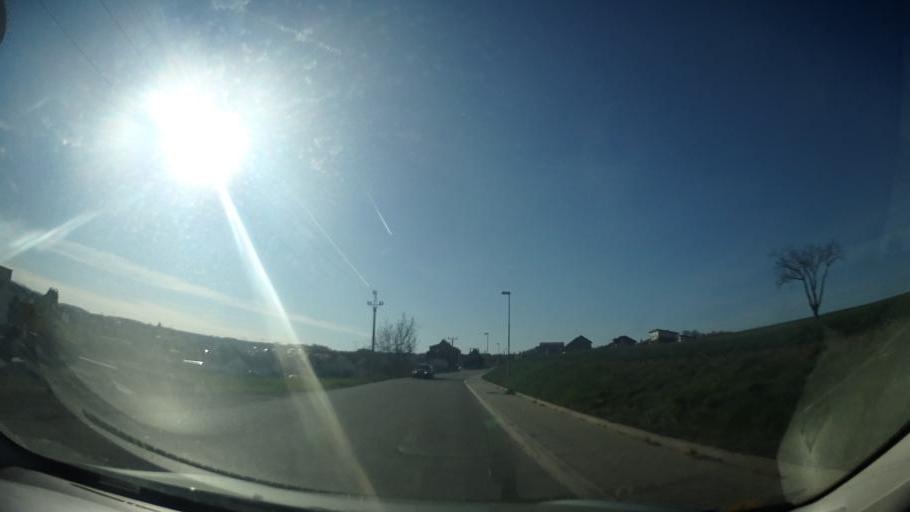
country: CZ
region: South Moravian
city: Moravany
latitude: 49.1457
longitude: 16.5859
